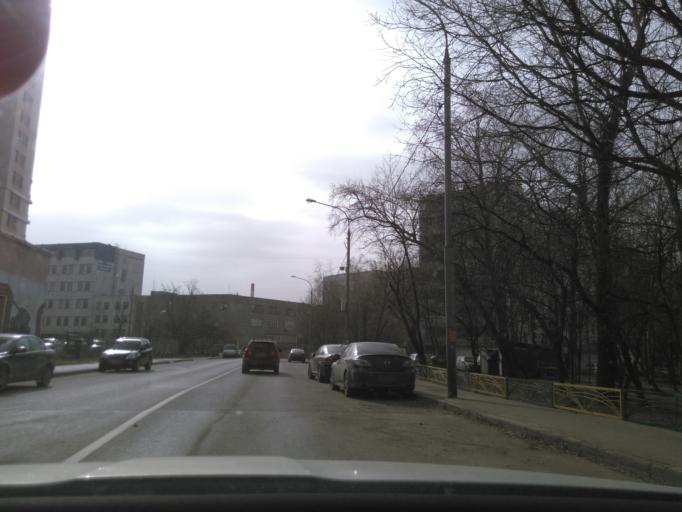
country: RU
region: Moskovskaya
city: Koptevo
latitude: 55.8222
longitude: 37.5186
